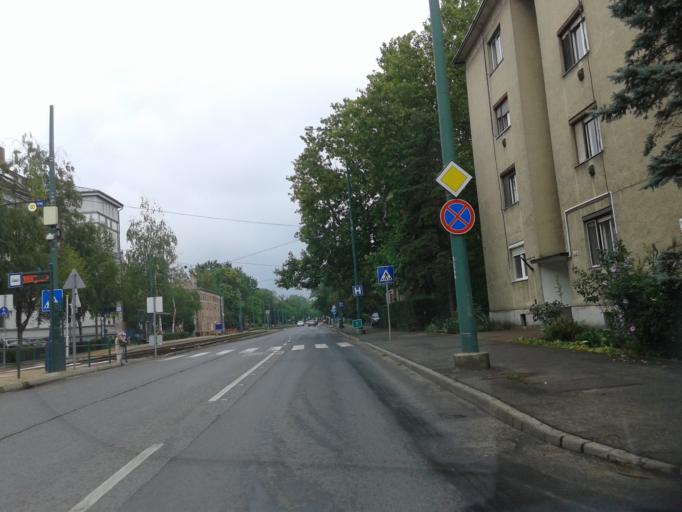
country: HU
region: Csongrad
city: Szeged
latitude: 46.2535
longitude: 20.1255
